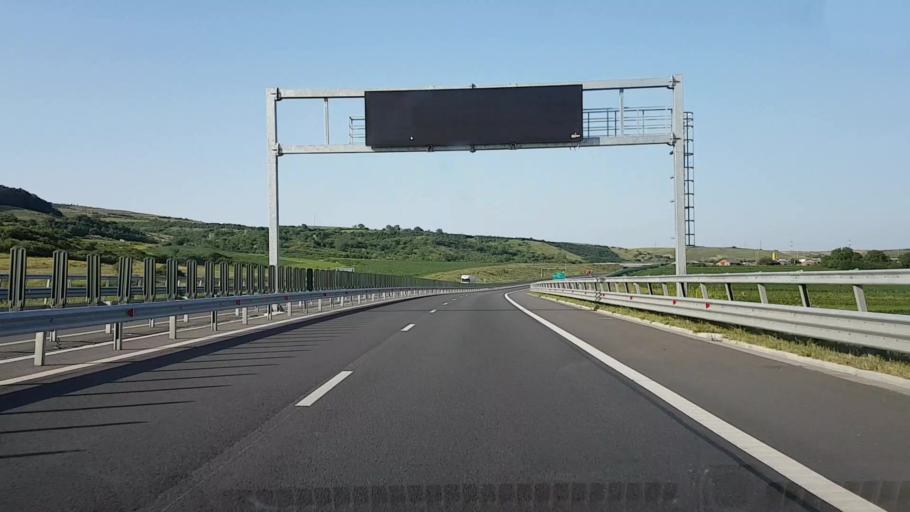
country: RO
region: Alba
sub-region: Comuna Miraslau
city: Miraslau
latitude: 46.3806
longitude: 23.7528
